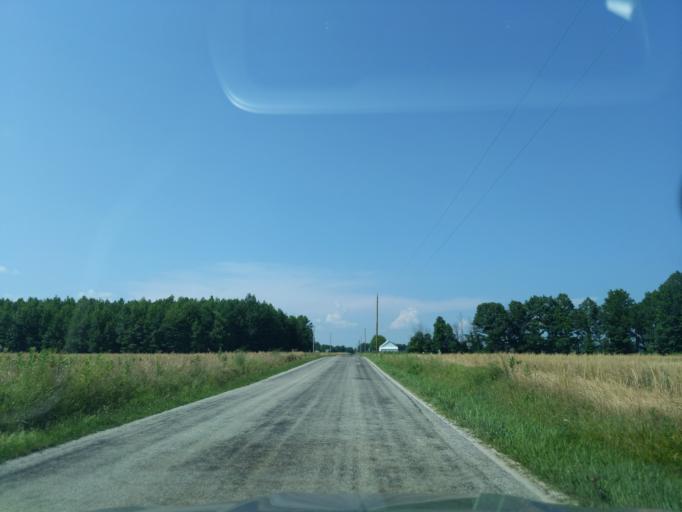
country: US
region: Indiana
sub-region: Ripley County
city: Osgood
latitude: 39.1389
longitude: -85.3397
